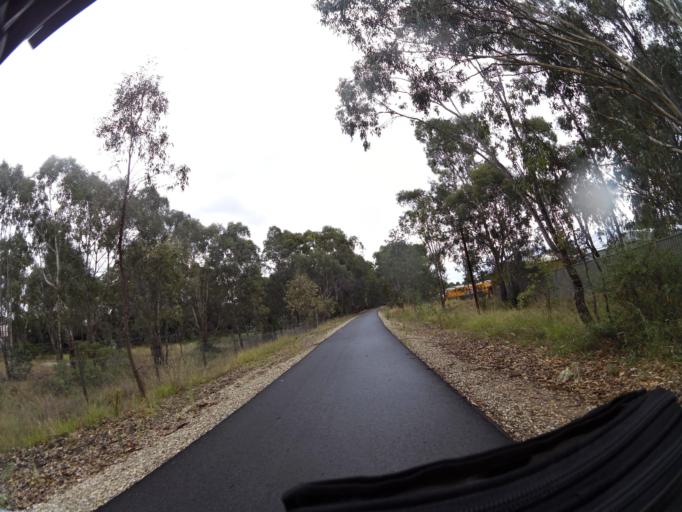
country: AU
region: Victoria
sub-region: Wodonga
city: Wodonga
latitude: -36.1343
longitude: 146.9008
